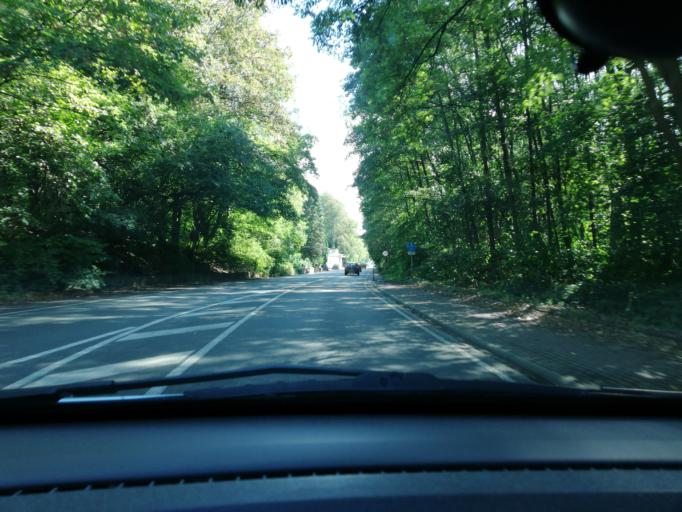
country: DE
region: North Rhine-Westphalia
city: Witten
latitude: 51.4223
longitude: 7.3539
